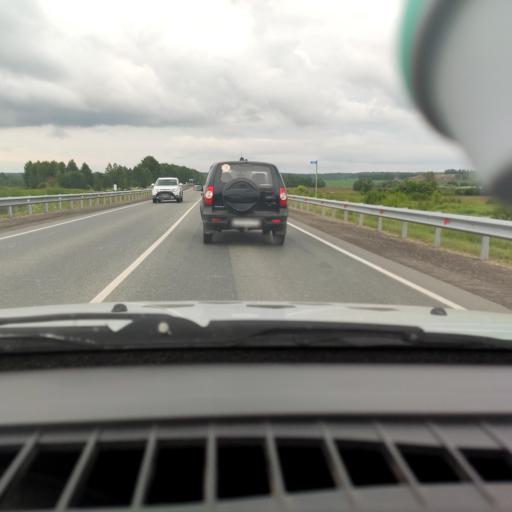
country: RU
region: Perm
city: Kukushtan
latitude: 57.4982
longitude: 56.6567
